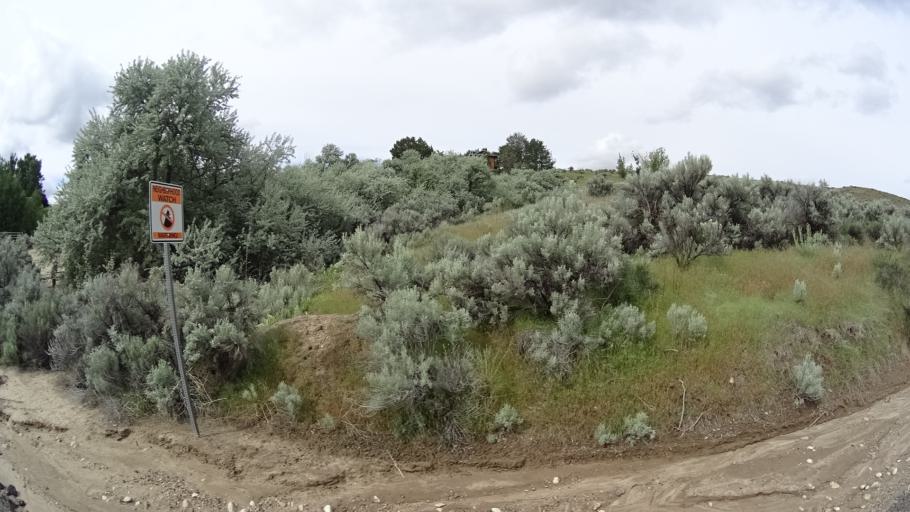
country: US
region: Idaho
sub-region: Ada County
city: Eagle
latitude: 43.7507
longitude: -116.3595
